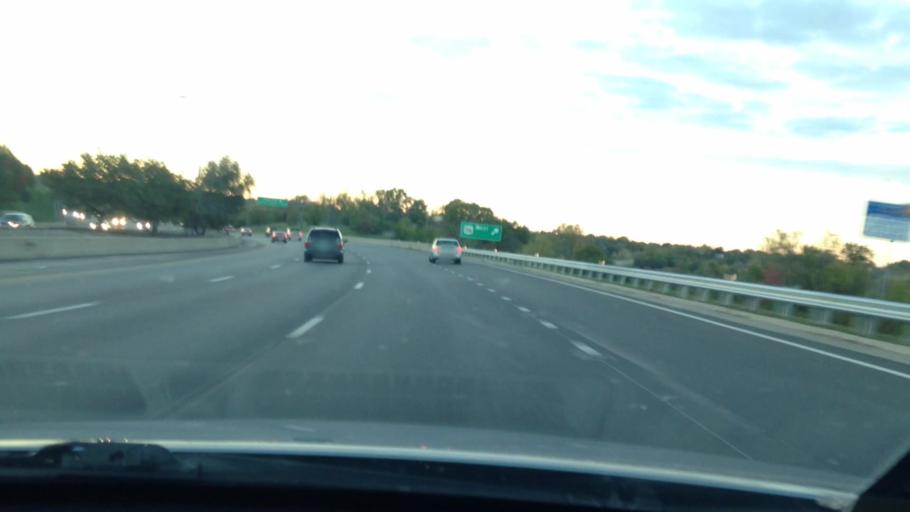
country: US
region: Kansas
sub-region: Johnson County
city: Westwood
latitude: 39.0358
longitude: -94.5537
